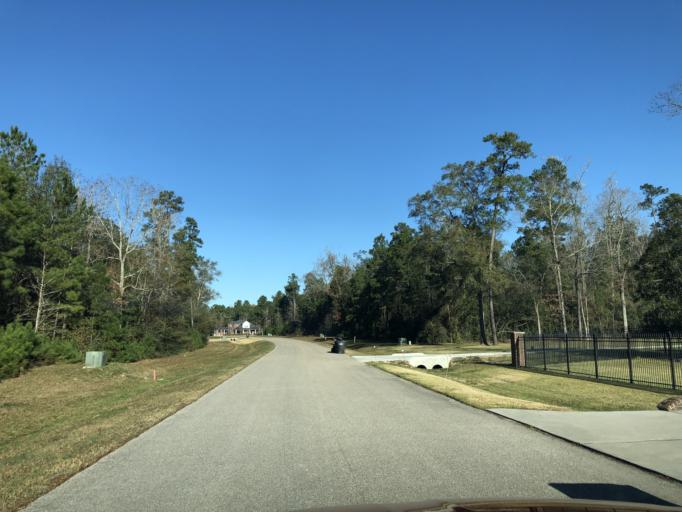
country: US
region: Texas
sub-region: Montgomery County
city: Porter Heights
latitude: 30.0654
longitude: -95.3222
